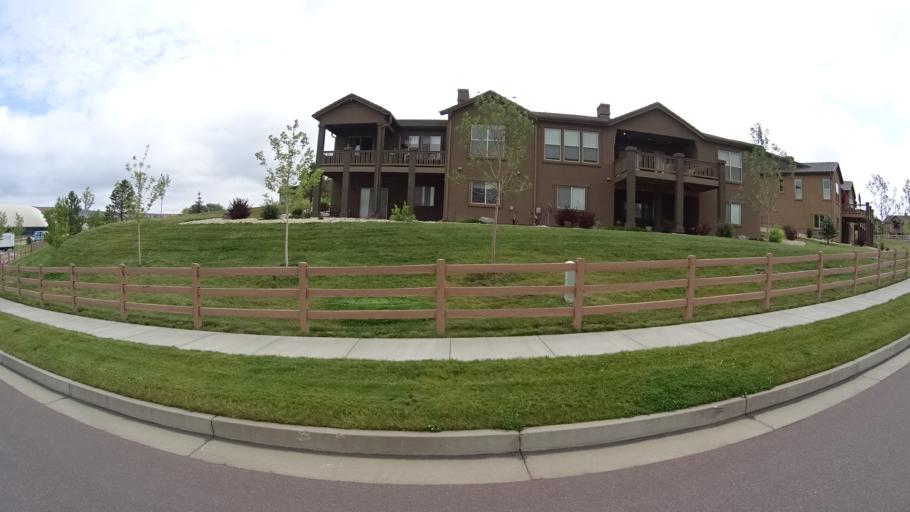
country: US
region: Colorado
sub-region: El Paso County
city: Gleneagle
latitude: 39.0163
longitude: -104.7896
